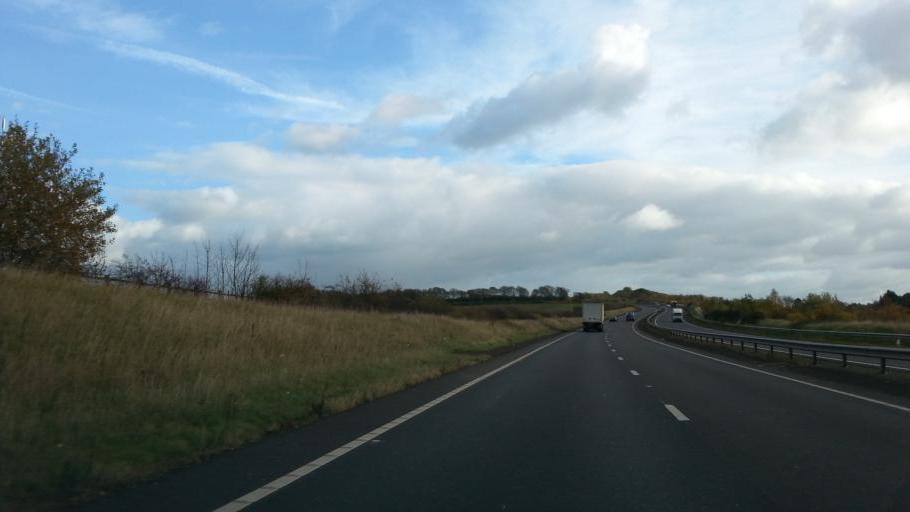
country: GB
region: England
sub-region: Staffordshire
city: Whittington
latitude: 52.6335
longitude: -1.7788
